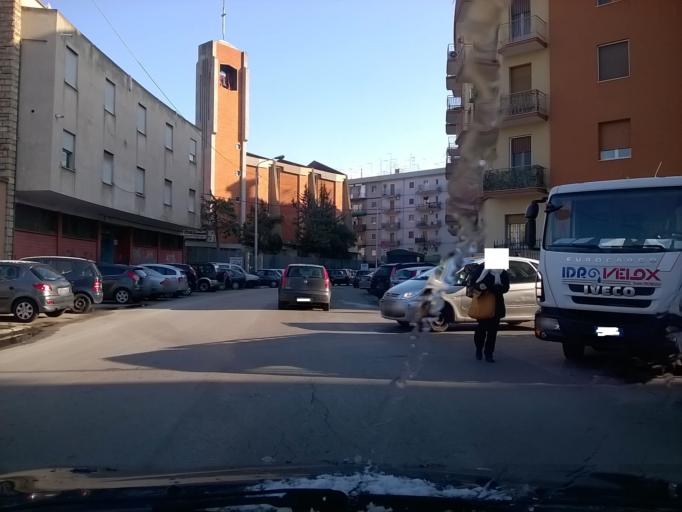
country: IT
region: Apulia
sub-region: Provincia di Taranto
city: Taranto
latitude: 40.4615
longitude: 17.2555
